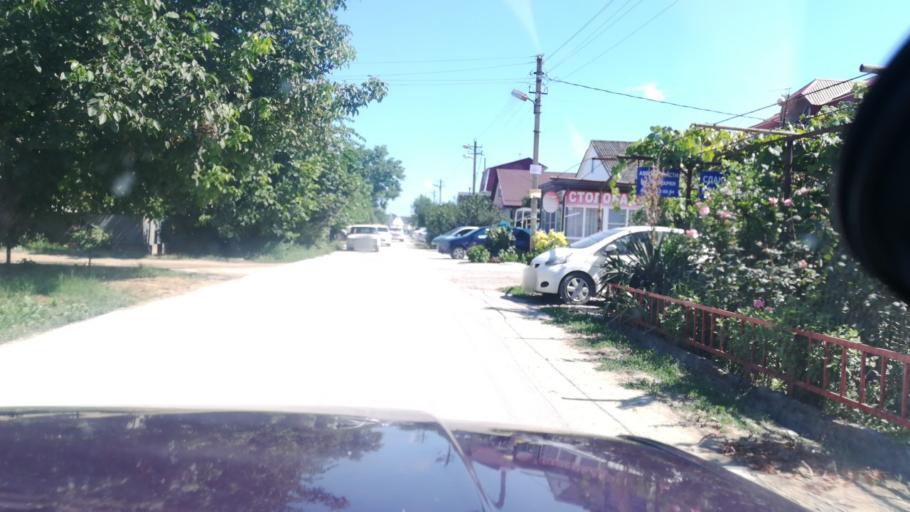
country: RU
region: Krasnodarskiy
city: Vityazevo
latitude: 44.9933
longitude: 37.2739
